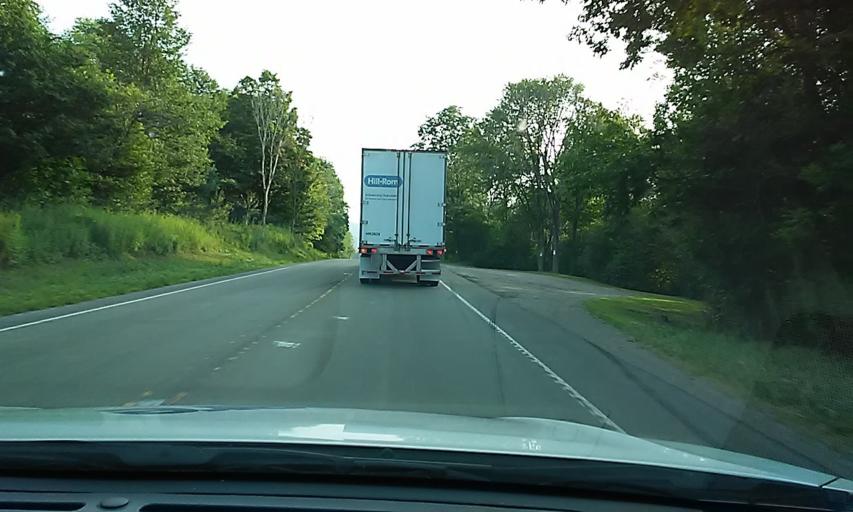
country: US
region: Pennsylvania
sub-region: McKean County
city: Smethport
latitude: 41.7426
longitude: -78.5318
